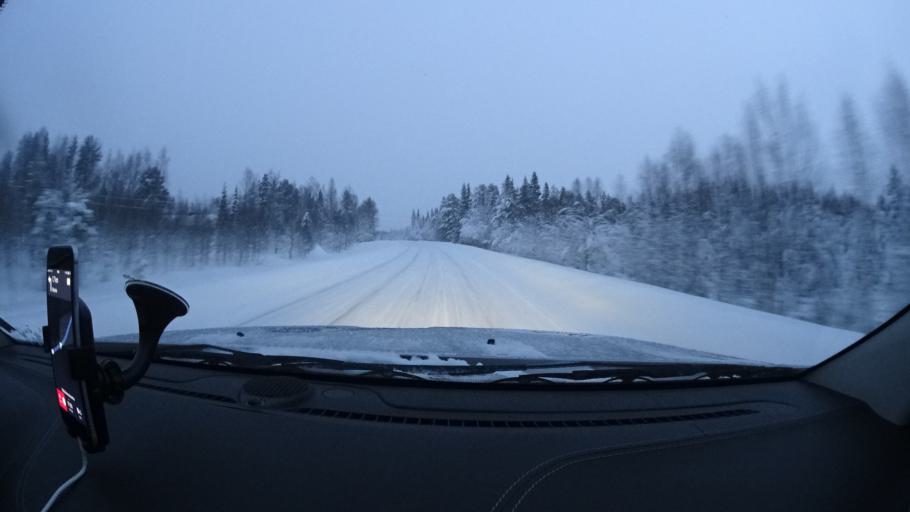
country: FI
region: Lapland
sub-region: Tunturi-Lappi
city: Kittilae
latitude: 67.6635
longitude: 24.8501
